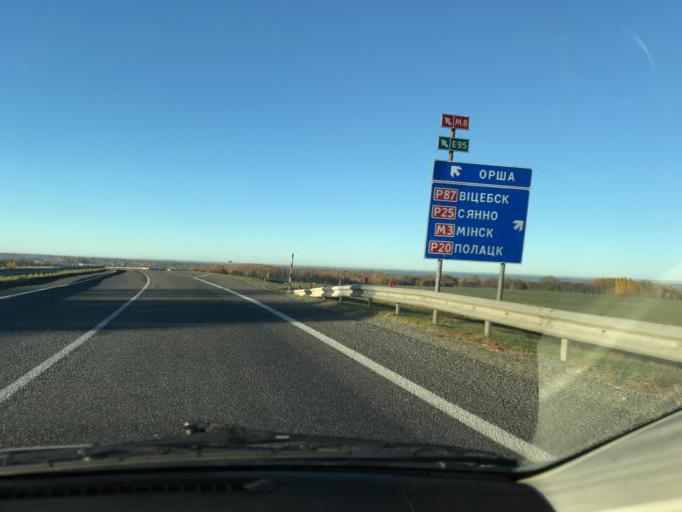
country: BY
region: Vitebsk
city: Vitebsk
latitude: 55.1068
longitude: 30.3050
